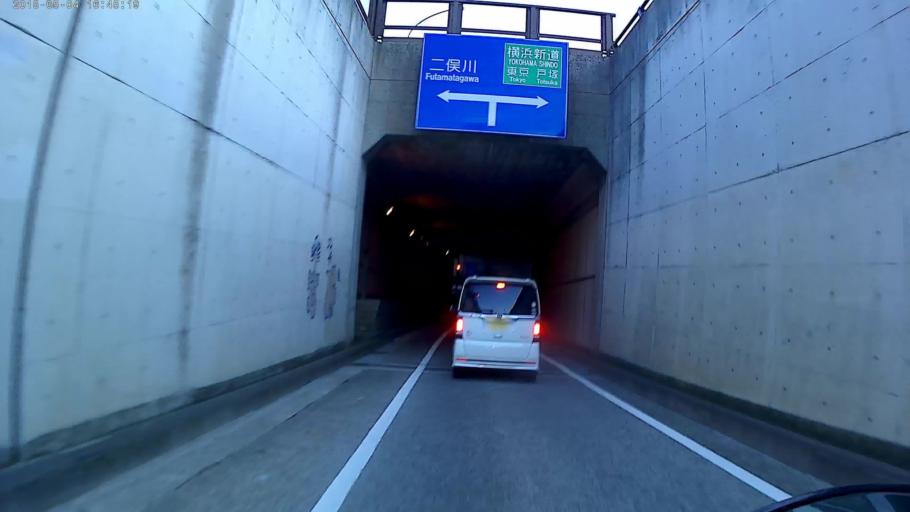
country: JP
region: Kanagawa
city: Yokohama
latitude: 35.4446
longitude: 139.5604
